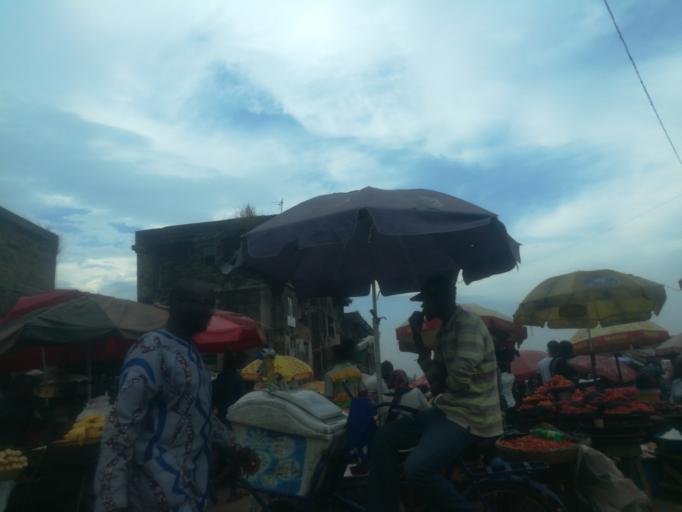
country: NG
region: Oyo
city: Ibadan
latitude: 7.4339
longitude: 3.9127
